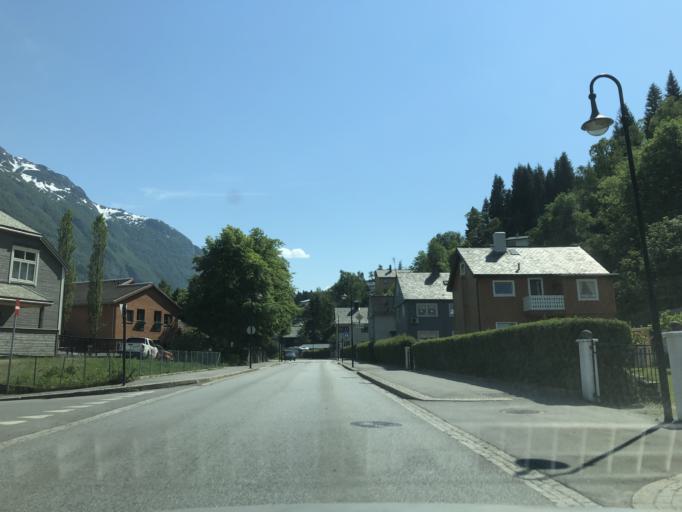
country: NO
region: Hordaland
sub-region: Odda
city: Odda
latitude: 60.0683
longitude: 6.5418
